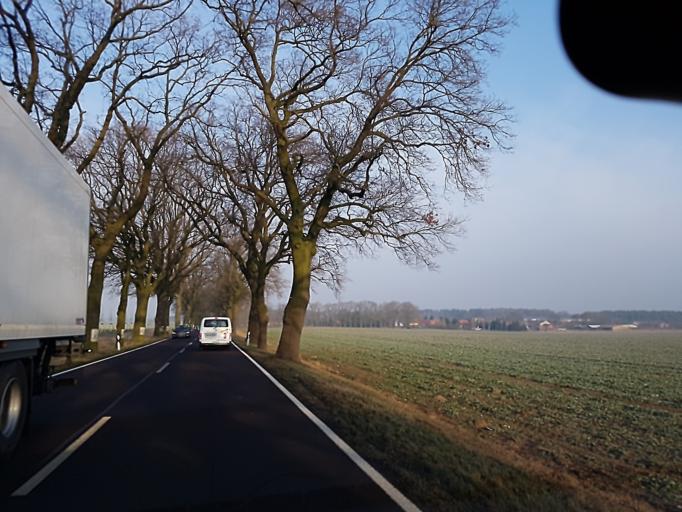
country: DE
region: Brandenburg
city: Gorzke
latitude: 52.1560
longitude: 12.3916
